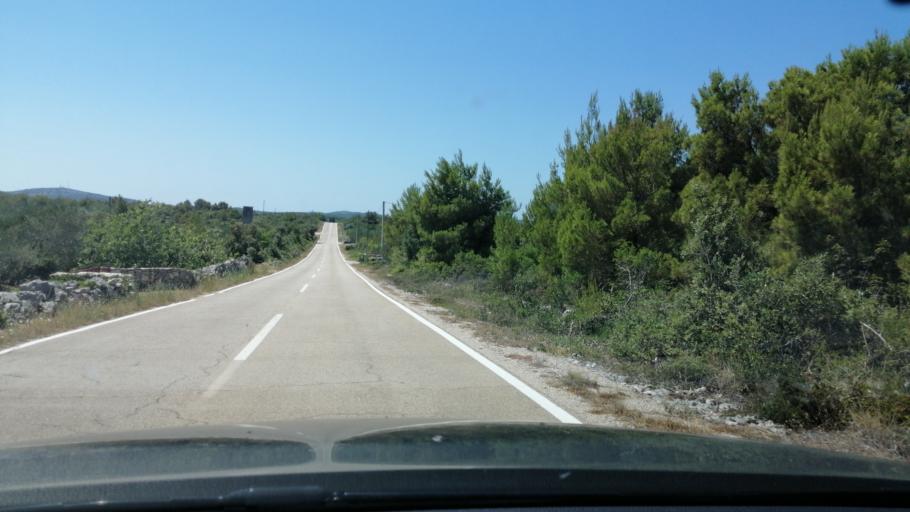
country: HR
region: Sibensko-Kniniska
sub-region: Grad Sibenik
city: Pirovac
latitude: 43.8355
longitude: 15.6872
